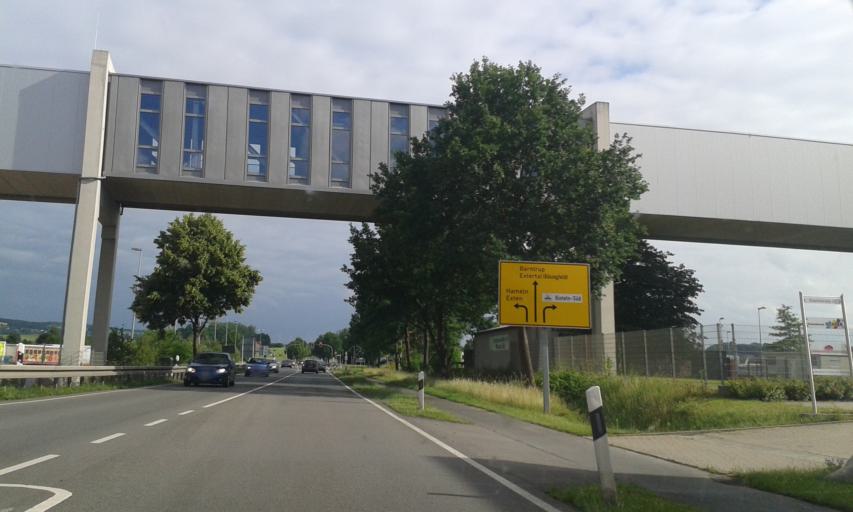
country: DE
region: Lower Saxony
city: Rinteln
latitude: 52.1714
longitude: 9.0843
